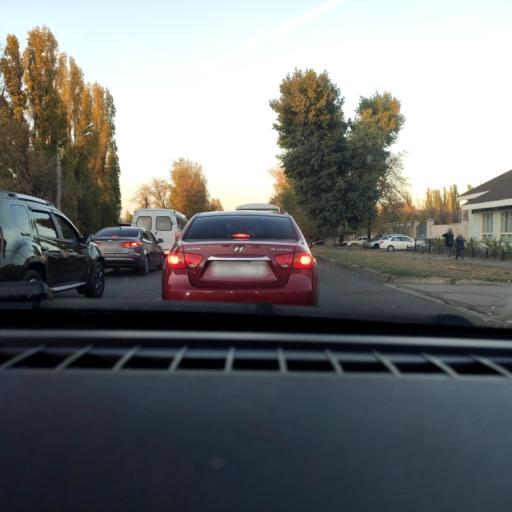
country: RU
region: Voronezj
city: Voronezh
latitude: 51.6529
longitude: 39.2717
